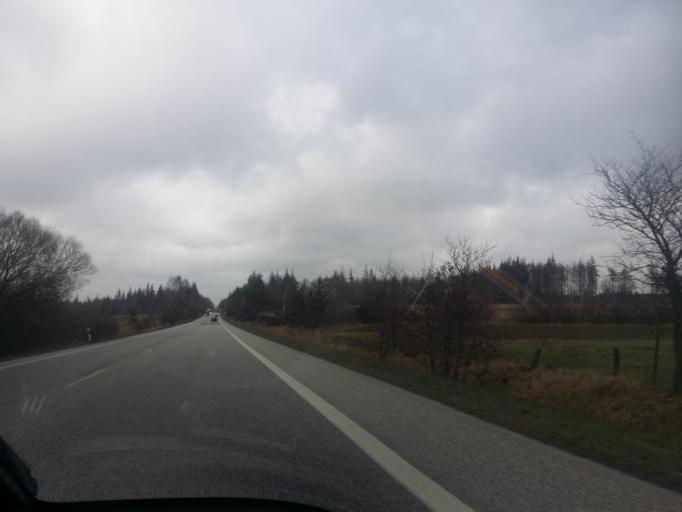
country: DE
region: Schleswig-Holstein
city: Bordelum
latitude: 54.6507
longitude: 8.9474
